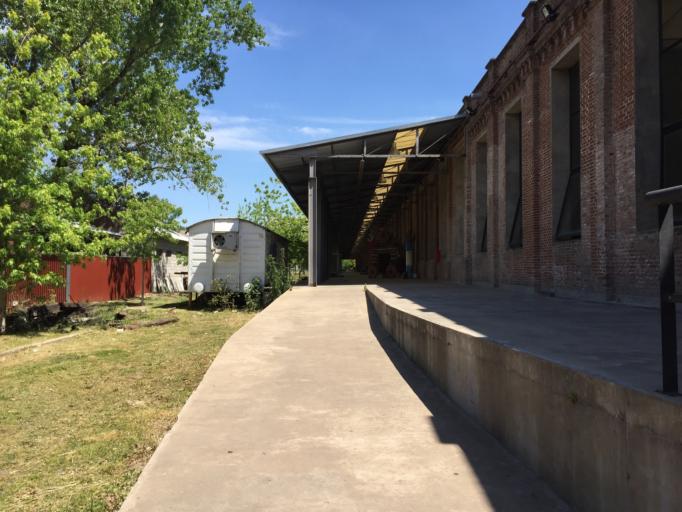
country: AR
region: Buenos Aires
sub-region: Partido de Lanus
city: Lanus
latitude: -34.7316
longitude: -58.3932
